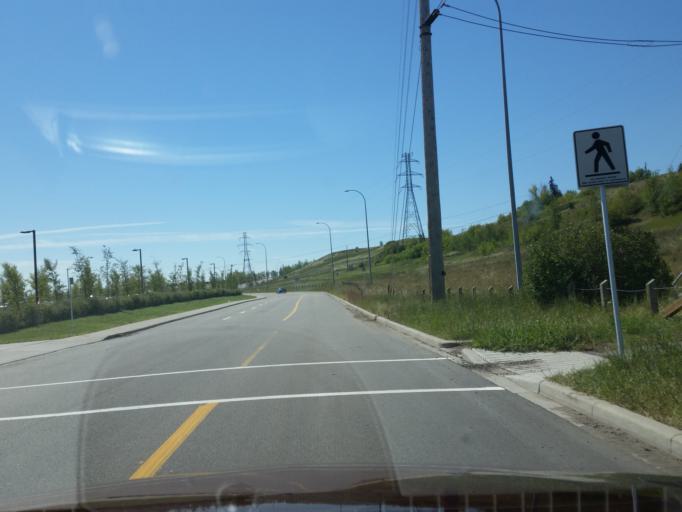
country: CA
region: Alberta
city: Calgary
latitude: 51.0554
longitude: -114.0266
